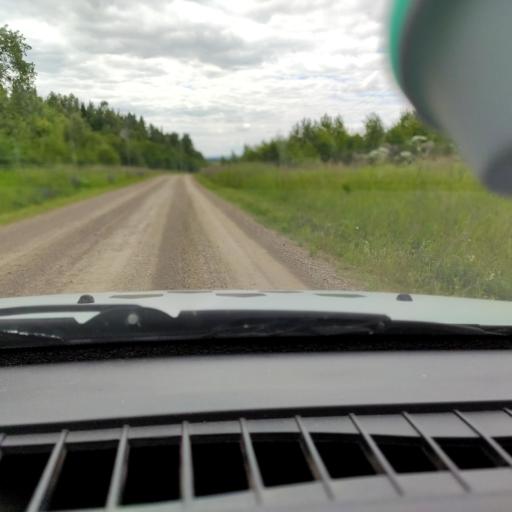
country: RU
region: Perm
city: Suksun
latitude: 57.1955
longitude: 57.5874
